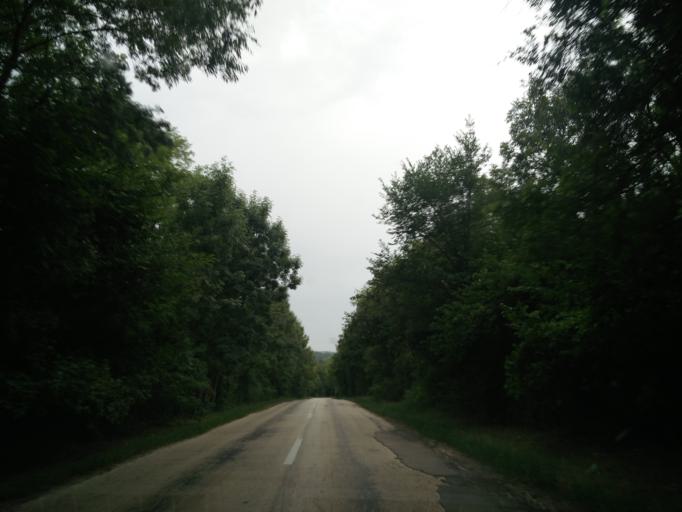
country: HU
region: Fejer
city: Etyek
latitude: 47.4377
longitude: 18.6945
